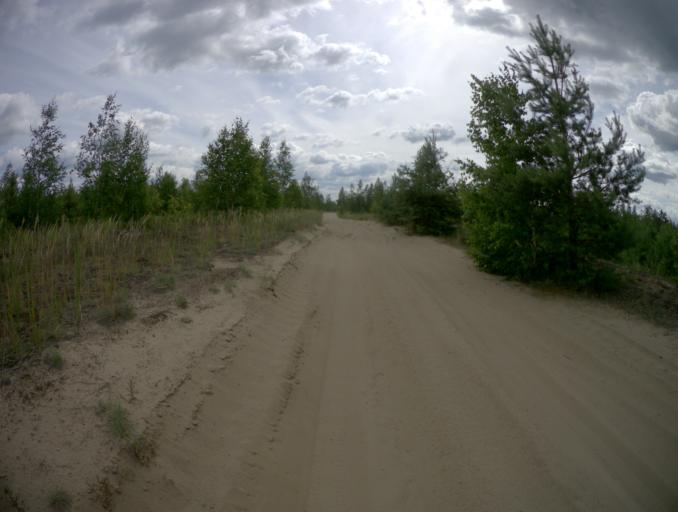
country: RU
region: Nizjnij Novgorod
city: Frolishchi
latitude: 56.5069
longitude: 42.5216
